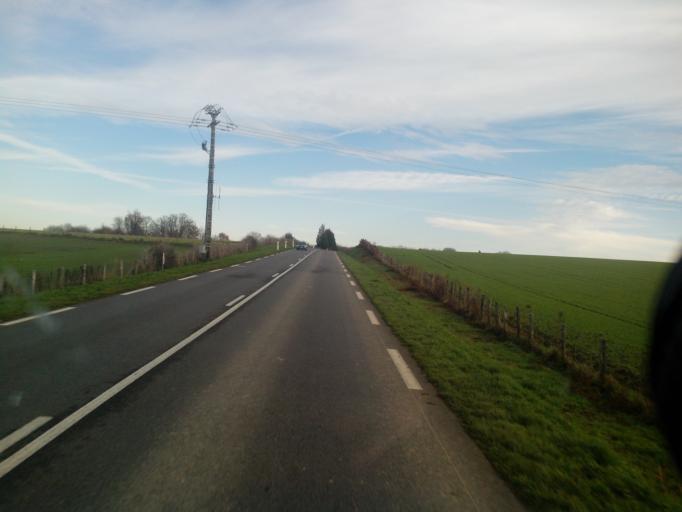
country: FR
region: Limousin
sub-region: Departement de la Haute-Vienne
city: Saint-Paul
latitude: 45.7923
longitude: 1.4546
